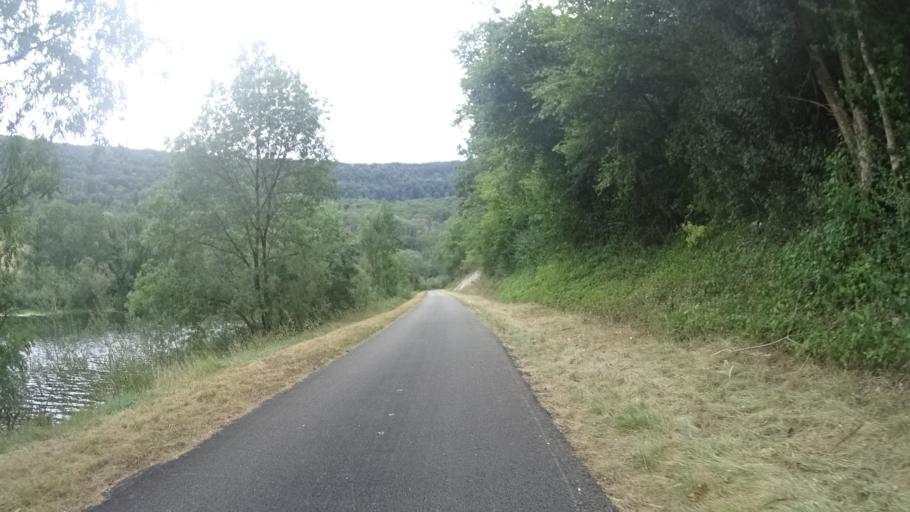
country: FR
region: Franche-Comte
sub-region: Departement du Doubs
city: Baume-les-Dames
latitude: 47.3338
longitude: 6.3135
